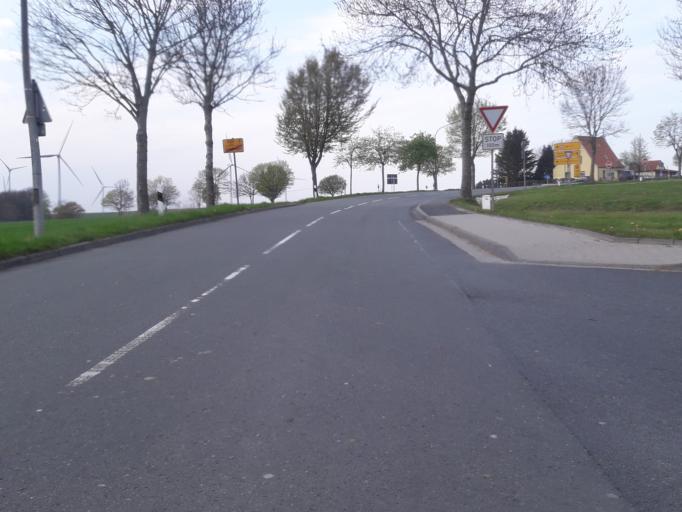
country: DE
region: North Rhine-Westphalia
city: Lichtenau
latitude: 51.6762
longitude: 8.8317
